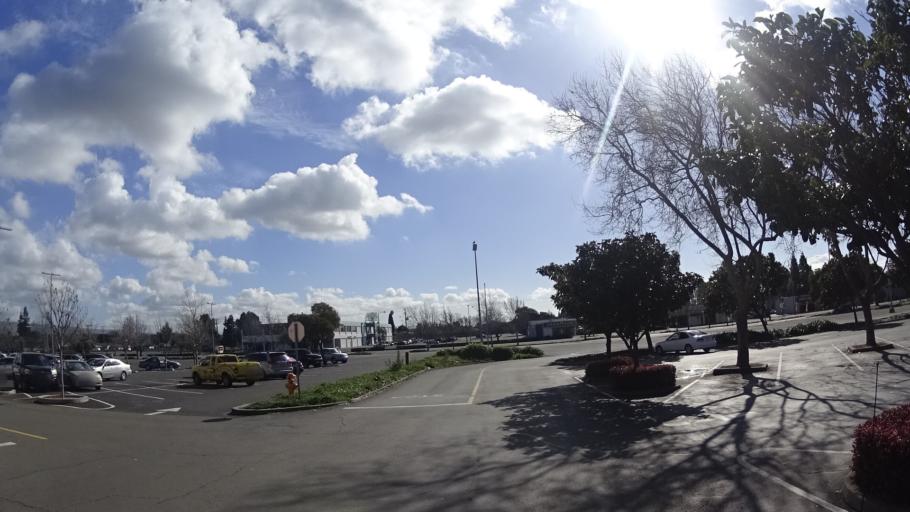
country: US
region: California
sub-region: Alameda County
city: Cherryland
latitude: 37.6497
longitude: -122.1047
